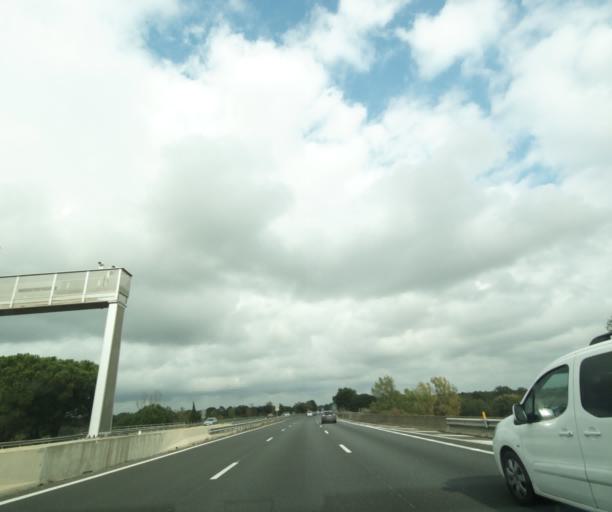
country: FR
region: Languedoc-Roussillon
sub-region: Departement de l'Herault
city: Cers
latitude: 43.3551
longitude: 3.3376
